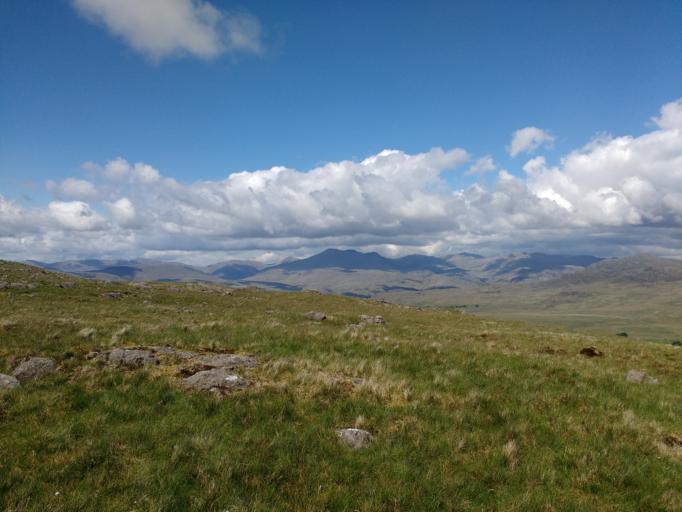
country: GB
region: England
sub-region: Cumbria
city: Millom
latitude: 54.3459
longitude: -3.2979
